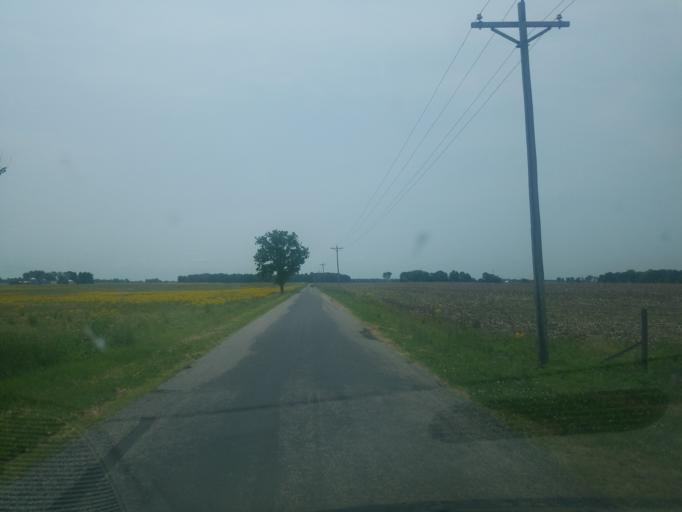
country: US
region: Ohio
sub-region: Marion County
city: Marion
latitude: 40.6514
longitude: -83.1979
